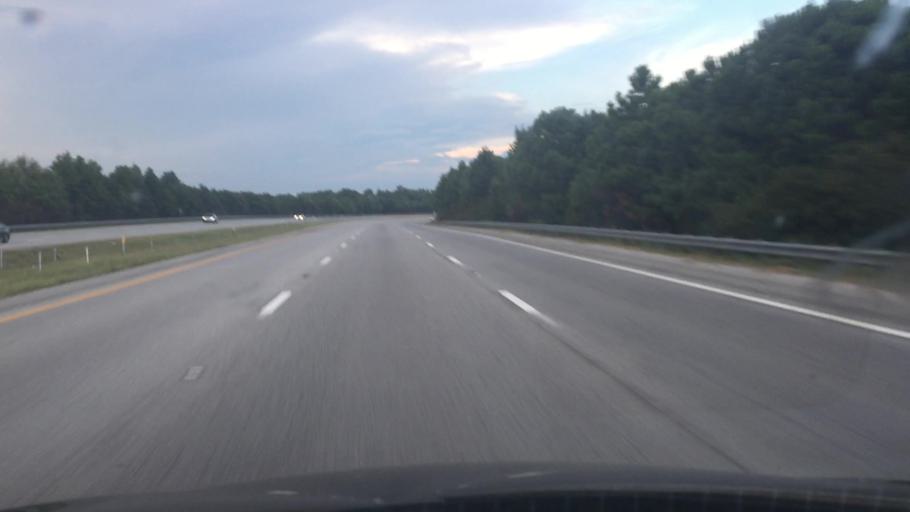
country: US
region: South Carolina
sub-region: Horry County
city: North Myrtle Beach
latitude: 33.8221
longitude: -78.7361
